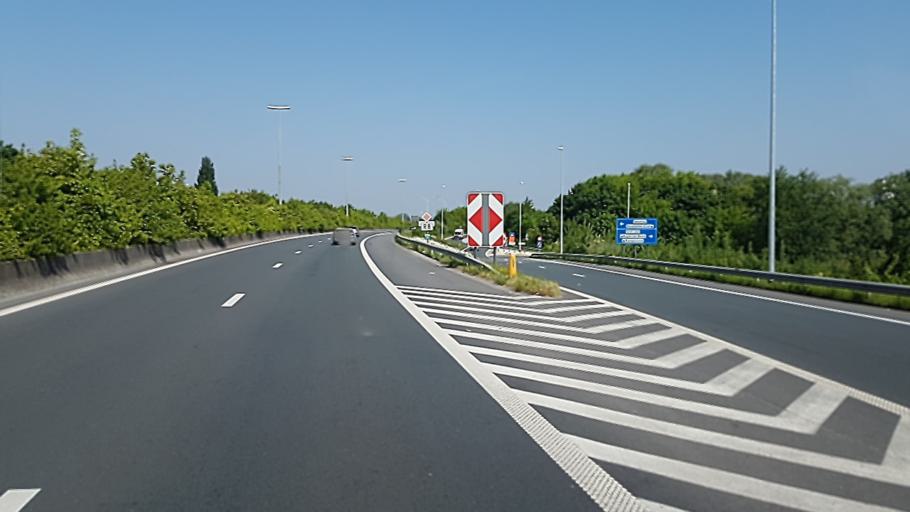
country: BE
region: Flanders
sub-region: Provincie West-Vlaanderen
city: Kuurne
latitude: 50.8263
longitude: 3.2954
